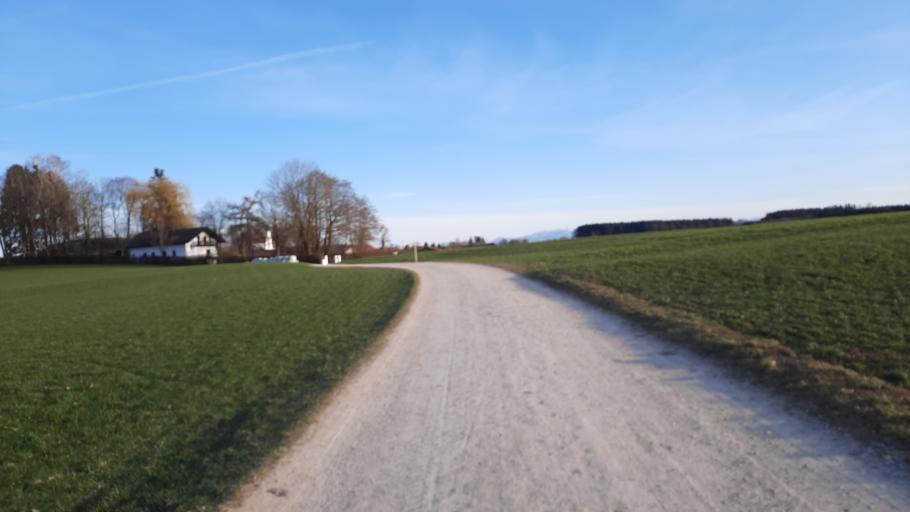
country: DE
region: Bavaria
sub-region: Upper Bavaria
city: Ebersberg
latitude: 48.0833
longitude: 11.9341
